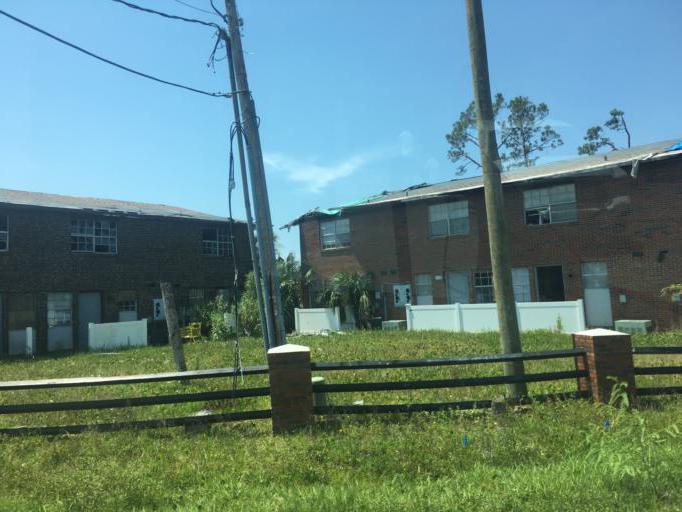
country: US
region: Florida
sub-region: Bay County
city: Lynn Haven
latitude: 30.2205
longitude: -85.6486
